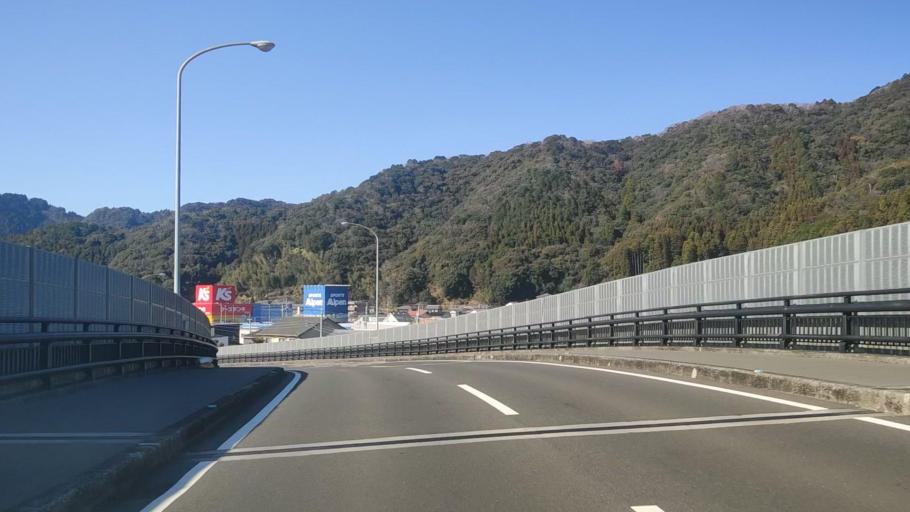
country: JP
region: Oita
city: Saiki
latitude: 32.9603
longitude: 131.8708
